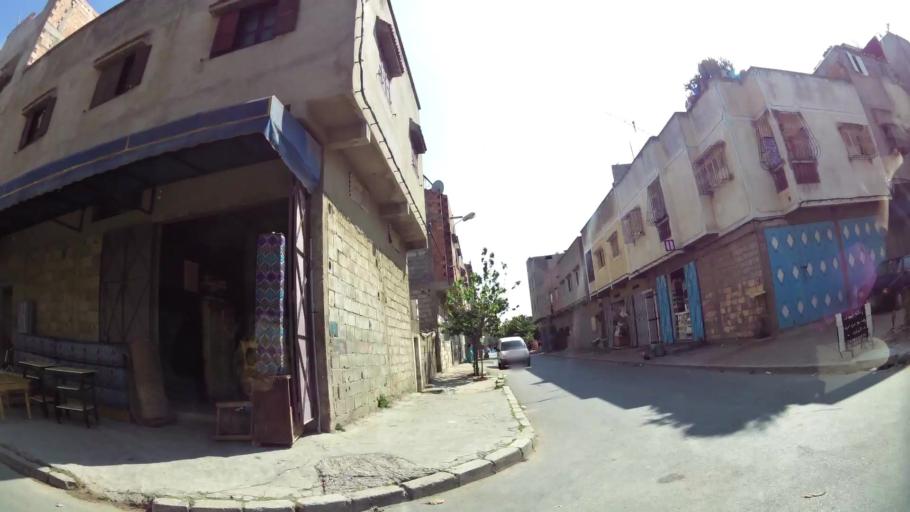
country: MA
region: Rabat-Sale-Zemmour-Zaer
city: Sale
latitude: 34.0689
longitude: -6.7726
